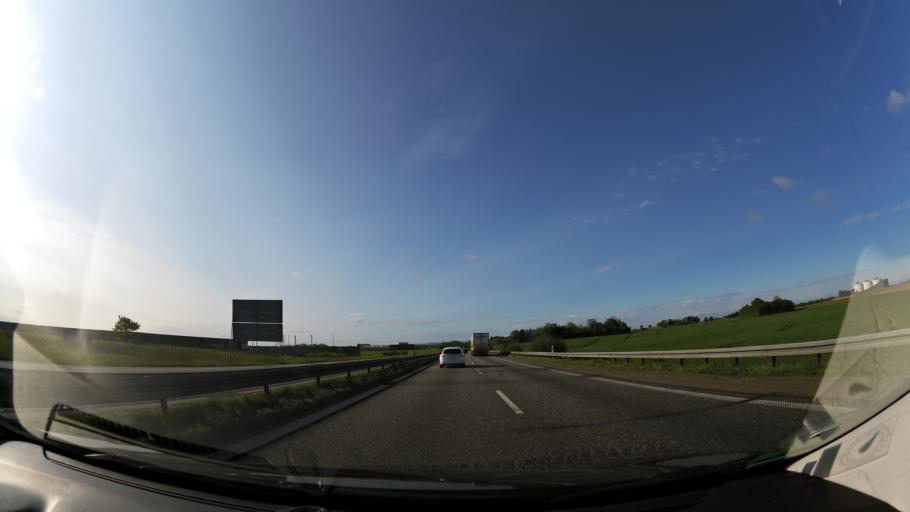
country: DK
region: Central Jutland
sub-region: Horsens Kommune
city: Horsens
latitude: 55.9269
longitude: 9.8198
